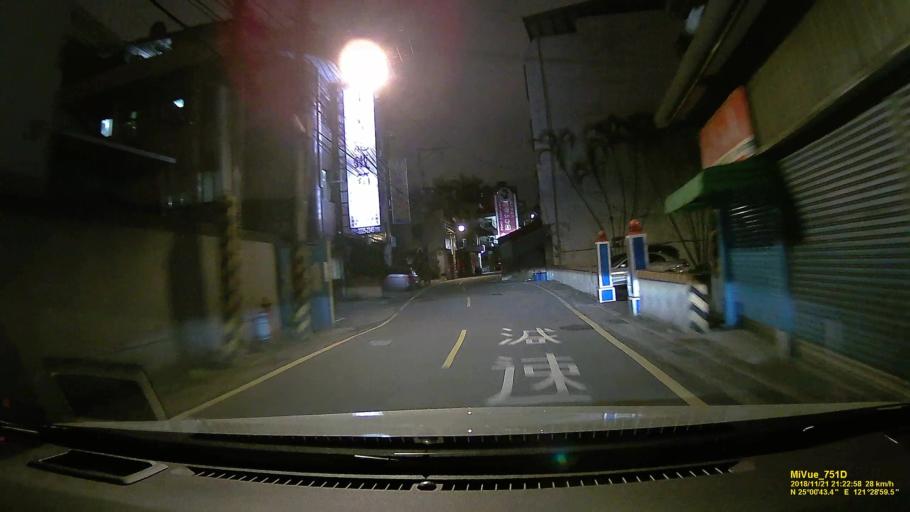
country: TW
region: Taipei
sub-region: Taipei
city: Banqiao
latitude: 25.0121
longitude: 121.4830
